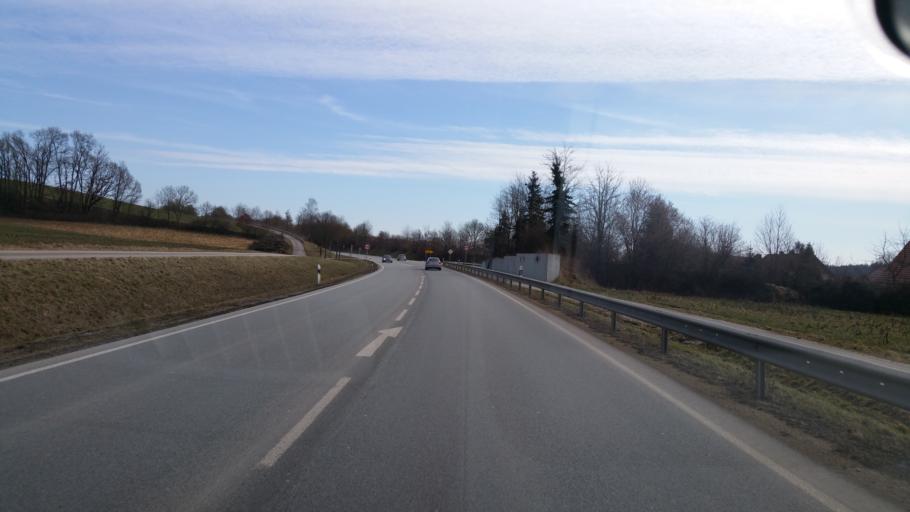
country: DE
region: Bavaria
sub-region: Lower Bavaria
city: Weihmichl
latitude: 48.5786
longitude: 12.0705
